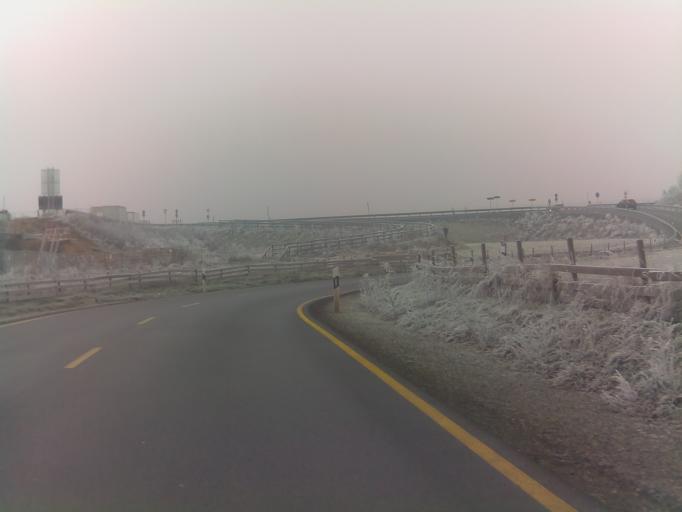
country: DE
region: Bavaria
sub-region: Regierungsbezirk Unterfranken
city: Hassfurt
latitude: 50.0268
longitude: 10.5061
